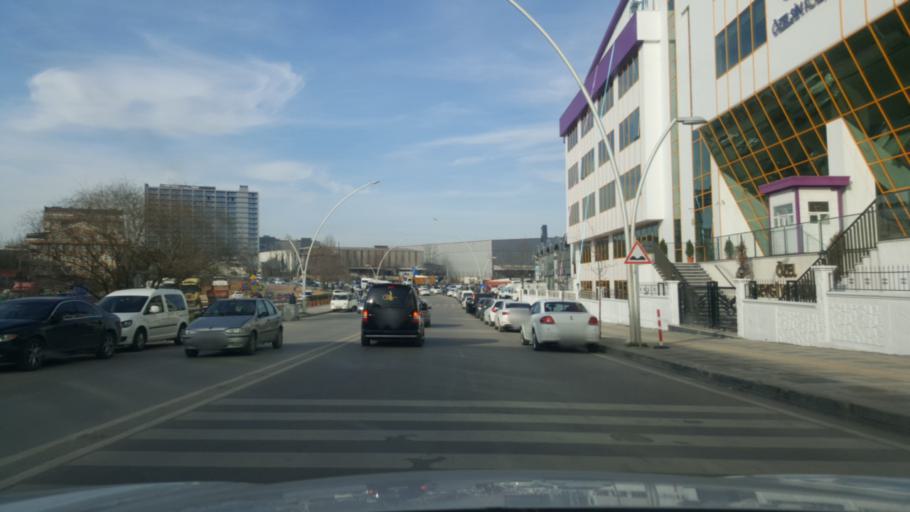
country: TR
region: Kocaeli
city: Gebze
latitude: 40.7893
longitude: 29.4418
